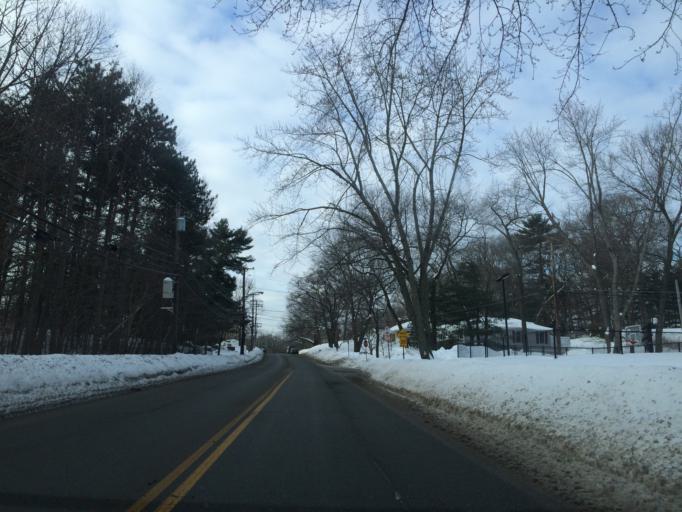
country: US
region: Massachusetts
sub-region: Middlesex County
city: Waltham
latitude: 42.3919
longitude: -71.2214
